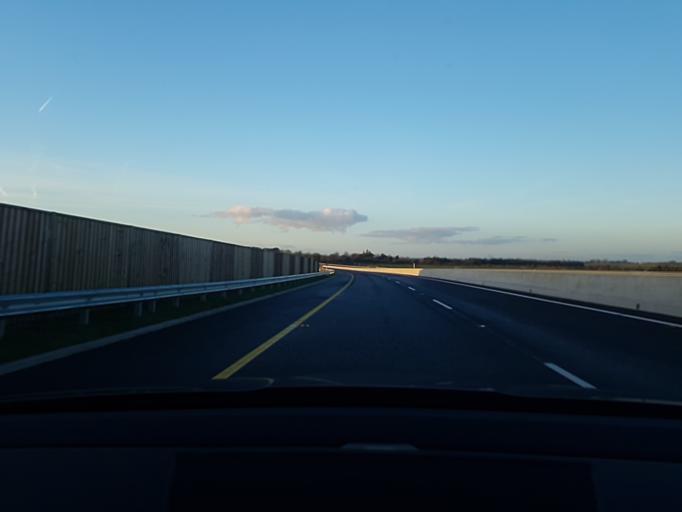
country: IE
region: Connaught
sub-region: County Galway
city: Tuam
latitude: 53.4577
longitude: -8.8482
